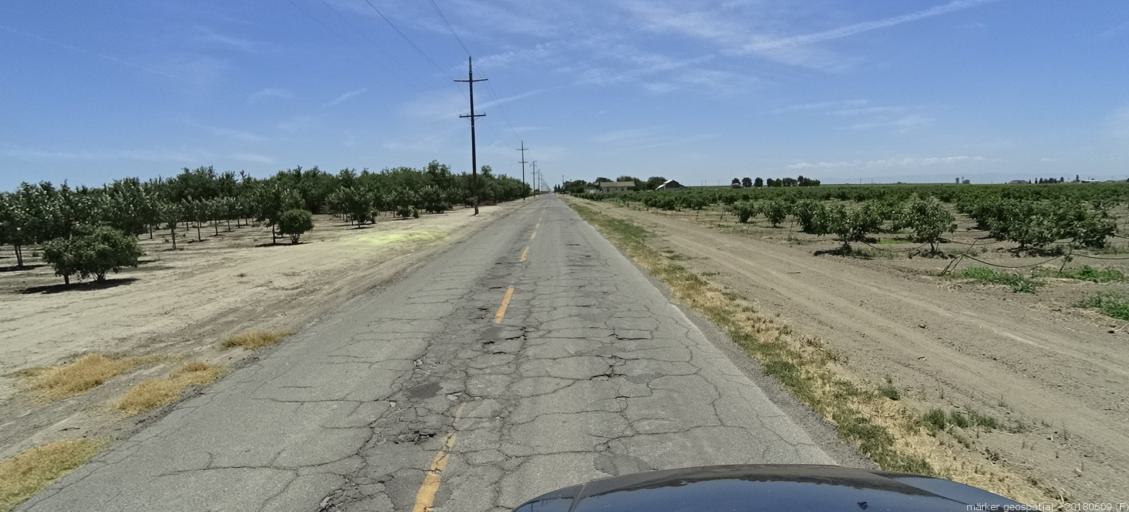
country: US
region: California
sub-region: Madera County
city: Parkwood
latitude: 36.8647
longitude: -120.1103
